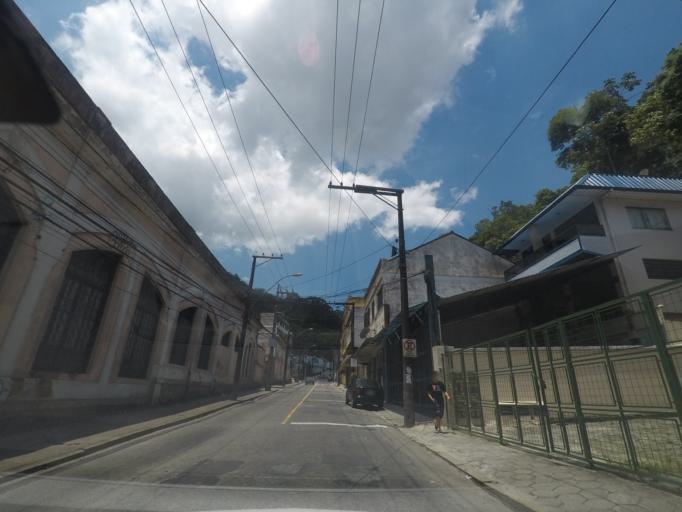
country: BR
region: Rio de Janeiro
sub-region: Petropolis
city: Petropolis
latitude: -22.5024
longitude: -43.1706
